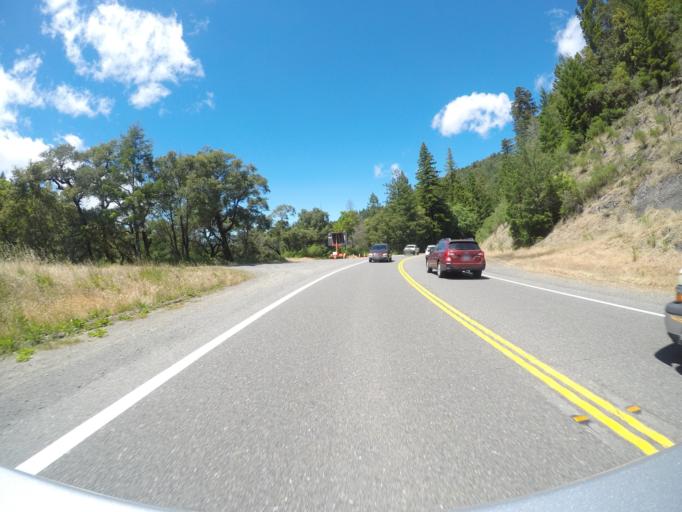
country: US
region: California
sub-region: Humboldt County
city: Redway
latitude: 39.9072
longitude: -123.7589
